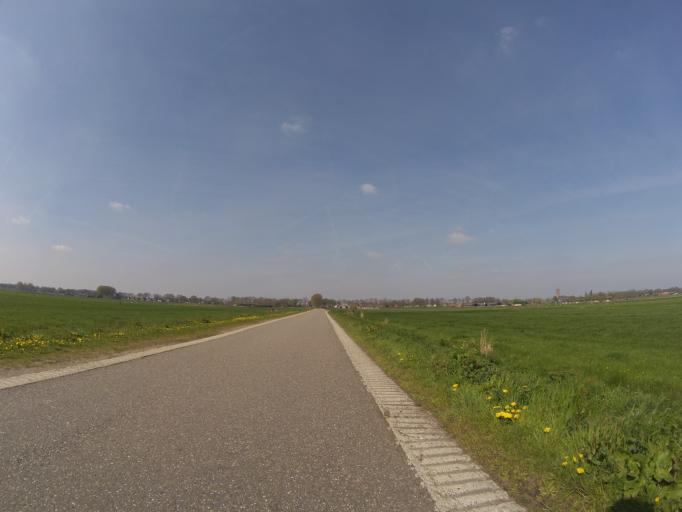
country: NL
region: Utrecht
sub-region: Gemeente Baarn
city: Baarn
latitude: 52.2454
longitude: 5.2753
